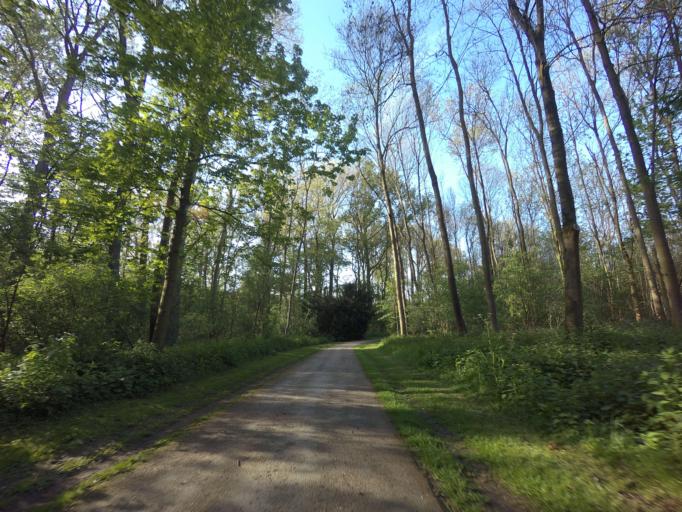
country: BE
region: Flanders
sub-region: Provincie Vlaams-Brabant
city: Grimbergen
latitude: 50.9168
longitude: 4.3884
